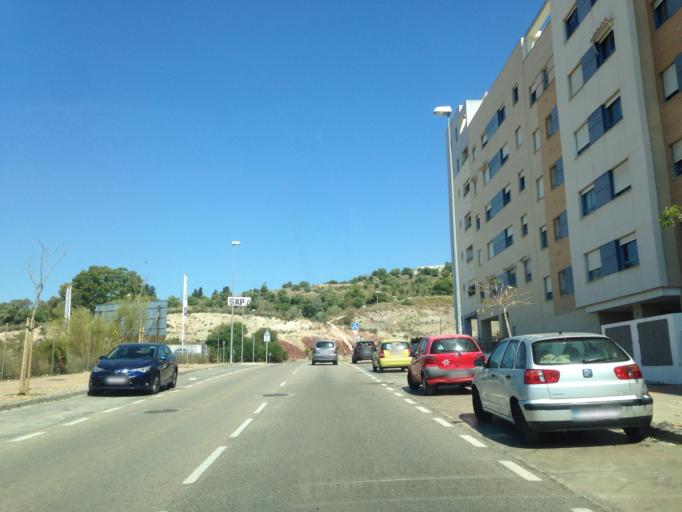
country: ES
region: Andalusia
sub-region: Provincia de Malaga
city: Malaga
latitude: 36.7248
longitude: -4.4844
